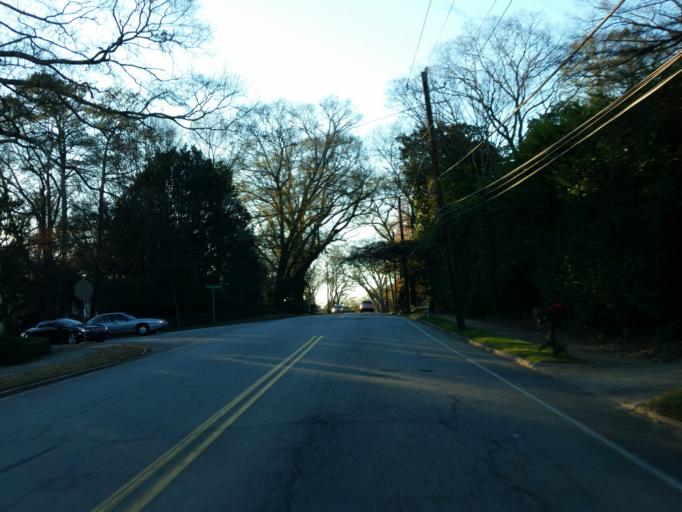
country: US
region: Georgia
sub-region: Fulton County
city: Atlanta
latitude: 33.8234
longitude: -84.3993
